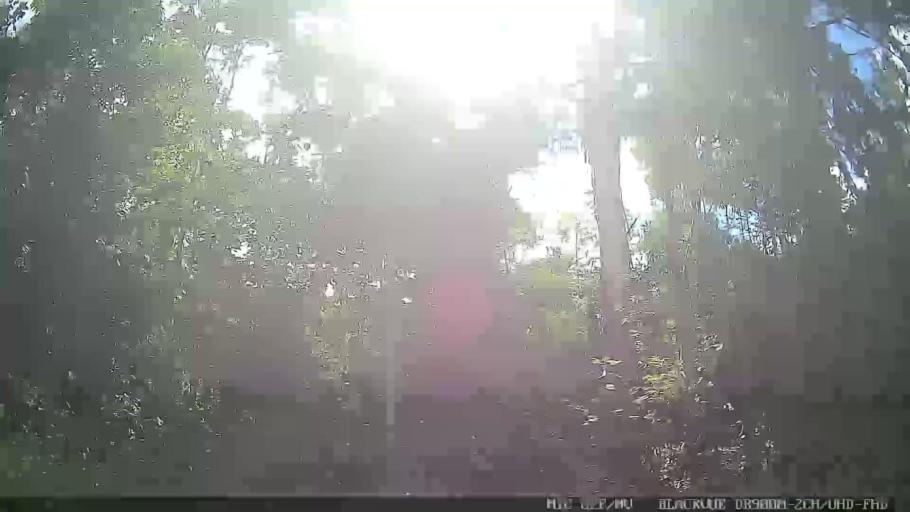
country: BR
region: Sao Paulo
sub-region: Caraguatatuba
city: Caraguatatuba
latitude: -23.5386
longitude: -45.5812
